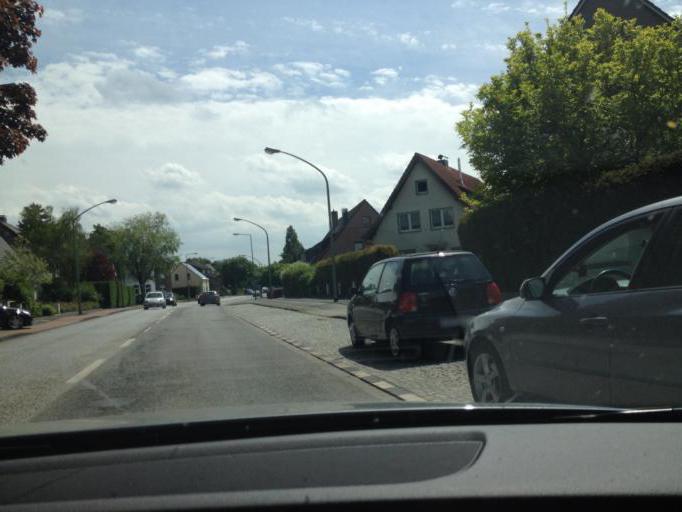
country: DE
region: North Rhine-Westphalia
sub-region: Regierungsbezirk Dusseldorf
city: Hochfeld
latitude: 51.3550
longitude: 6.7816
